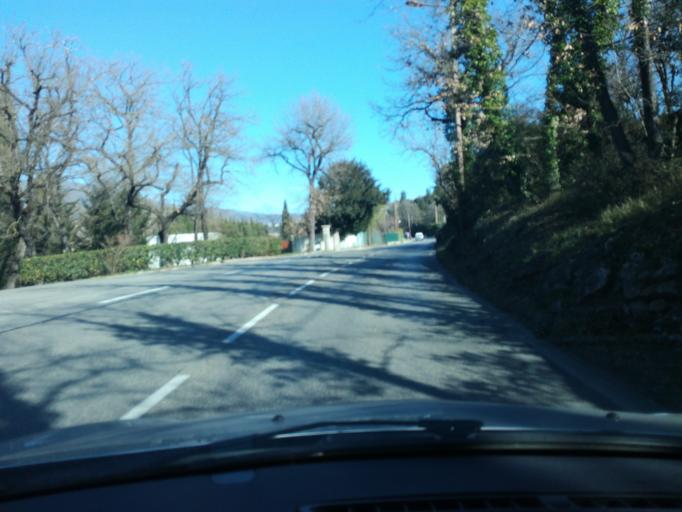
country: FR
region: Provence-Alpes-Cote d'Azur
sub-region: Departement des Alpes-Maritimes
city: Pegomas
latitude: 43.6331
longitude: 6.9312
